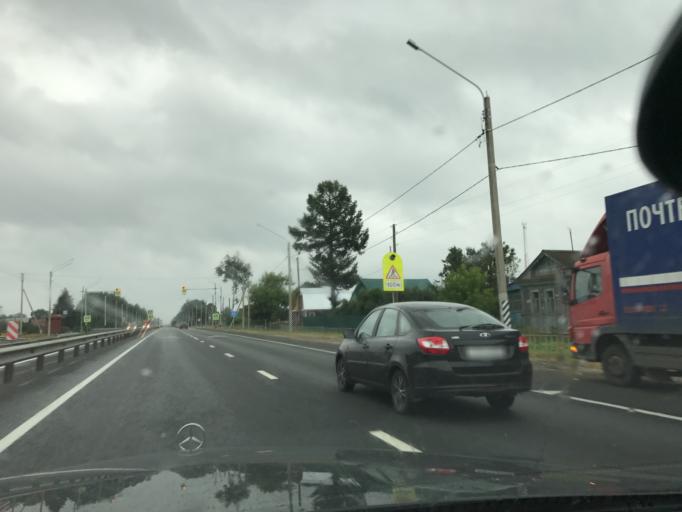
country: RU
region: Vladimir
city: Krasnyy Oktyabr'
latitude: 56.2193
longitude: 41.4812
